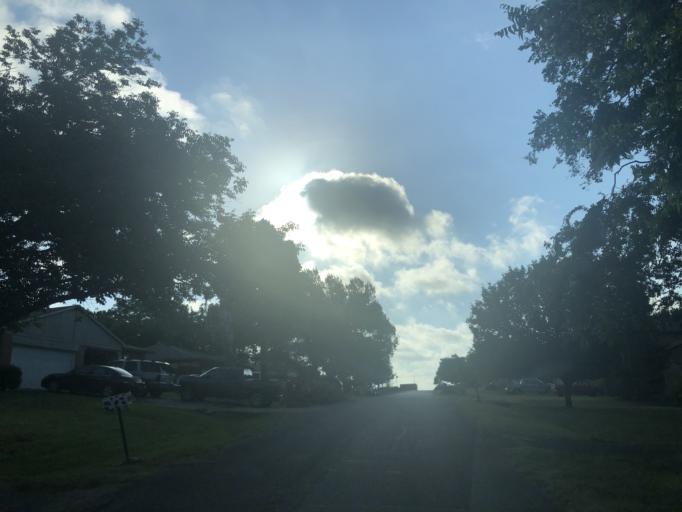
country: US
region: Texas
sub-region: Dallas County
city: Duncanville
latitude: 32.6700
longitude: -96.9111
